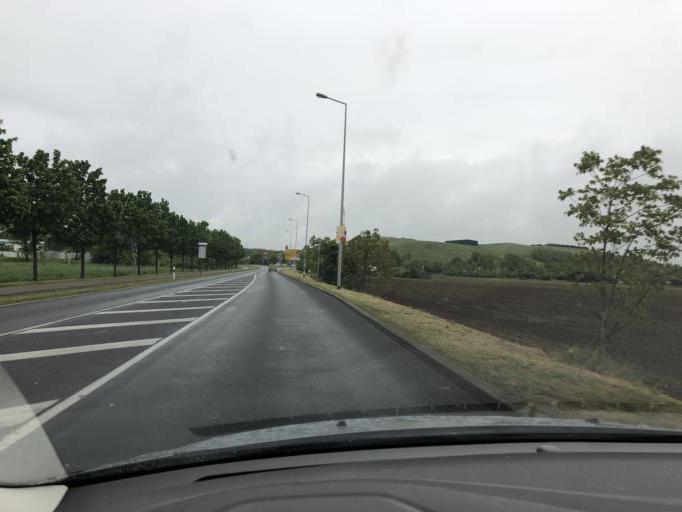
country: DE
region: Saxony-Anhalt
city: Dessau
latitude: 51.8131
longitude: 12.2156
